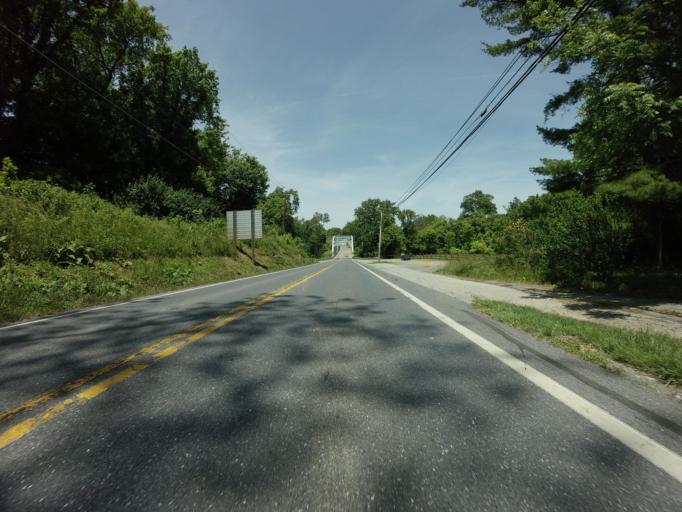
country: US
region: Maryland
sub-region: Frederick County
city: Bartonsville
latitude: 39.3680
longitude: -77.3894
